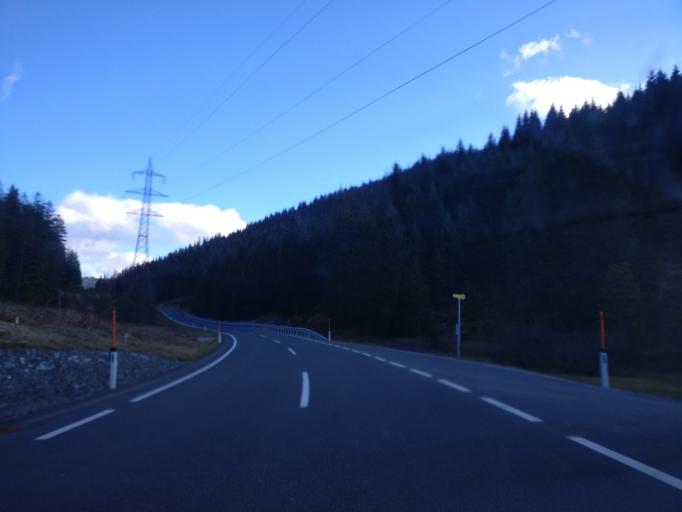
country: AT
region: Salzburg
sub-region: Politischer Bezirk Zell am See
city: Dienten am Hochkonig
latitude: 47.3996
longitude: 12.9957
